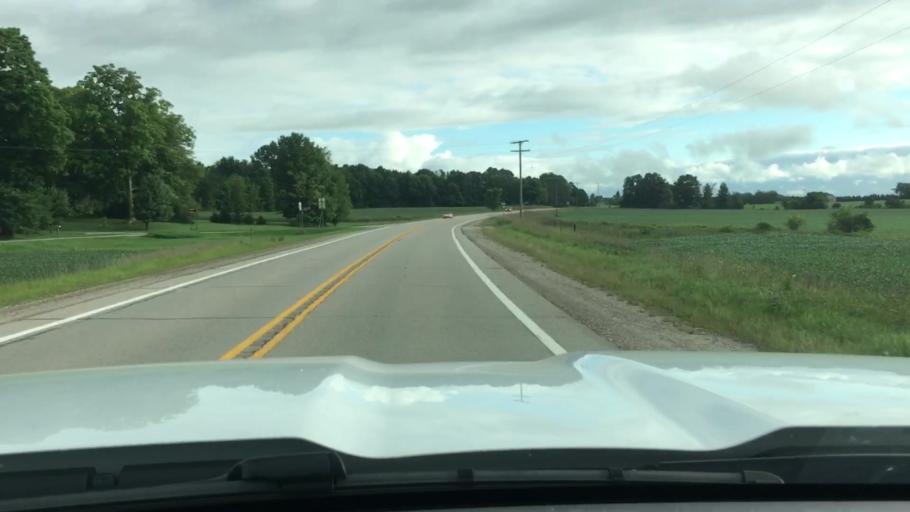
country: US
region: Michigan
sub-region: Tuscola County
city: Caro
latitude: 43.5357
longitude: -83.3434
